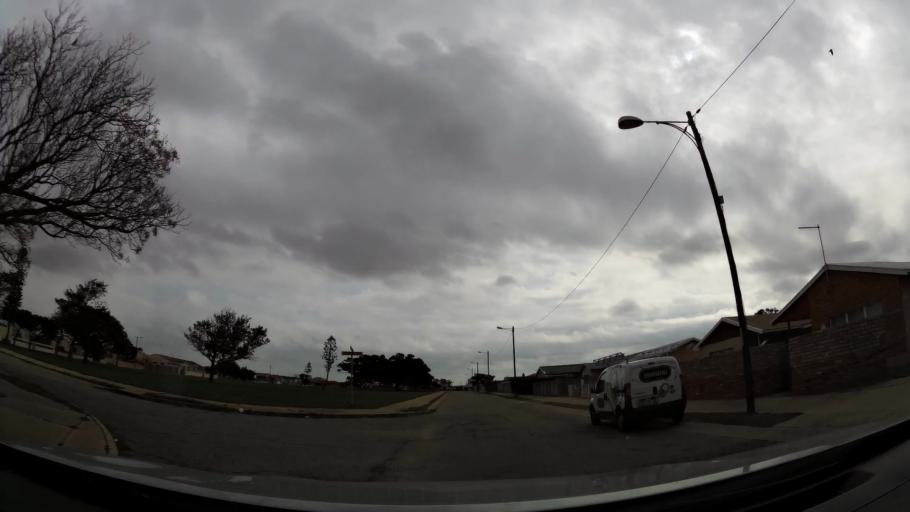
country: ZA
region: Eastern Cape
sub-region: Nelson Mandela Bay Metropolitan Municipality
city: Port Elizabeth
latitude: -33.9002
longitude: 25.5660
